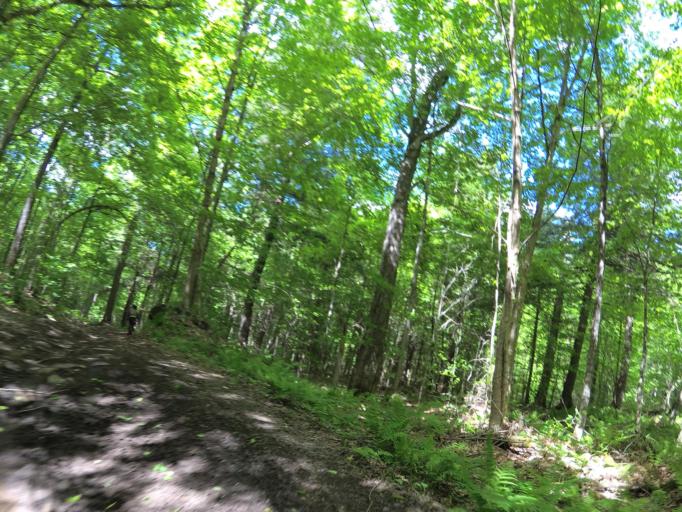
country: CA
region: Ontario
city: Renfrew
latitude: 45.0550
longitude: -76.8494
